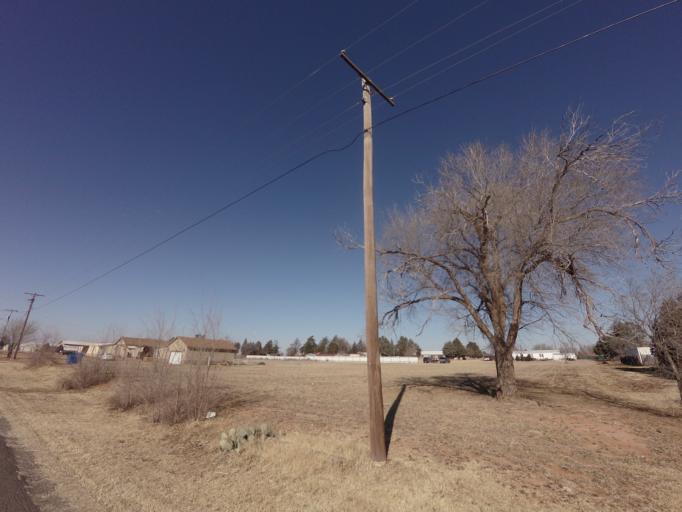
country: US
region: New Mexico
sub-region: Curry County
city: Clovis
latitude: 34.3757
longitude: -103.2029
